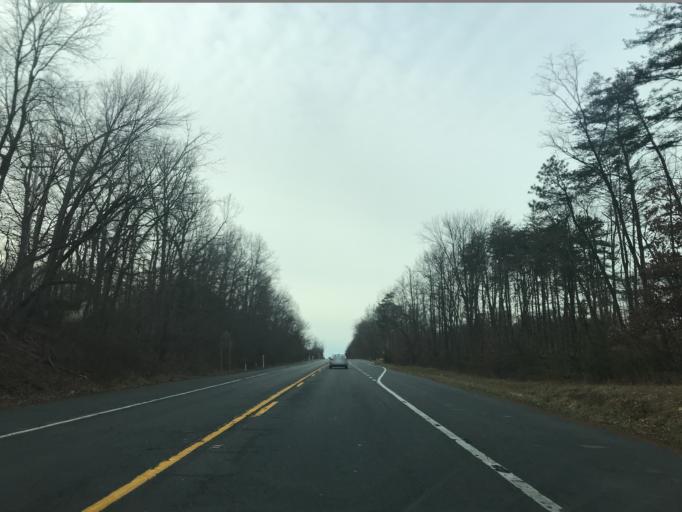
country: US
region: Maryland
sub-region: Cecil County
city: Elkton
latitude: 39.6171
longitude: -75.8005
